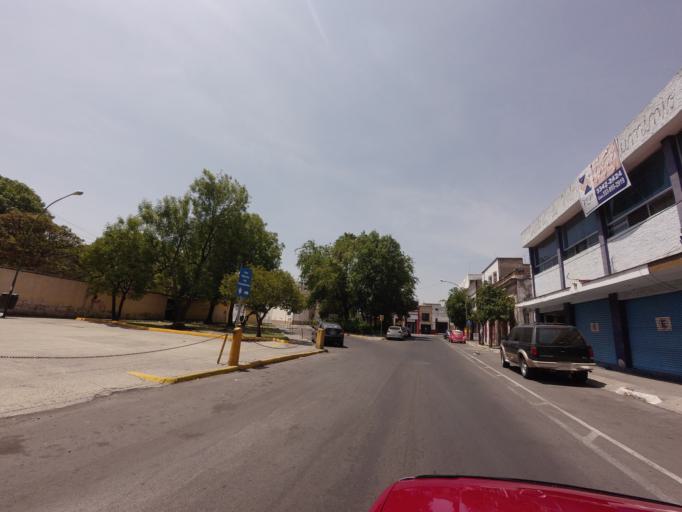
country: MX
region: Jalisco
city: Guadalajara
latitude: 20.6801
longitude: -103.3432
